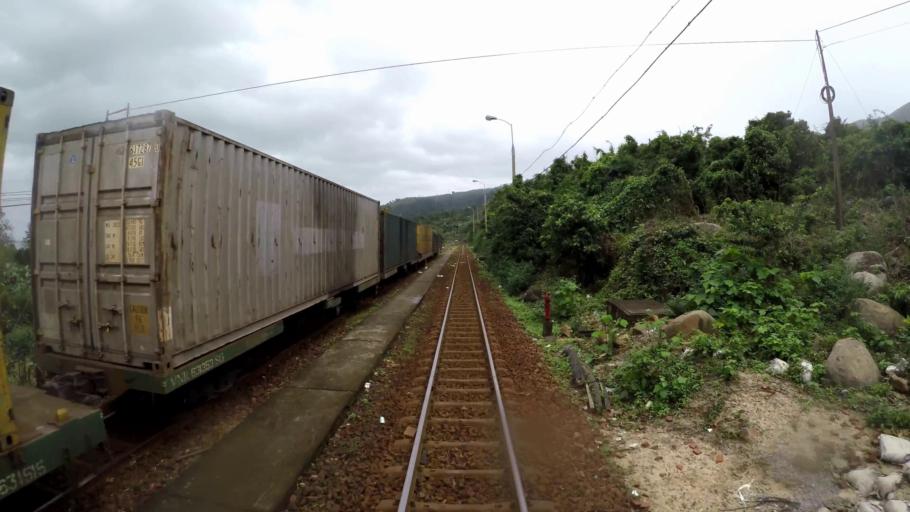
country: VN
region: Da Nang
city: Lien Chieu
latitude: 16.1668
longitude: 108.1361
